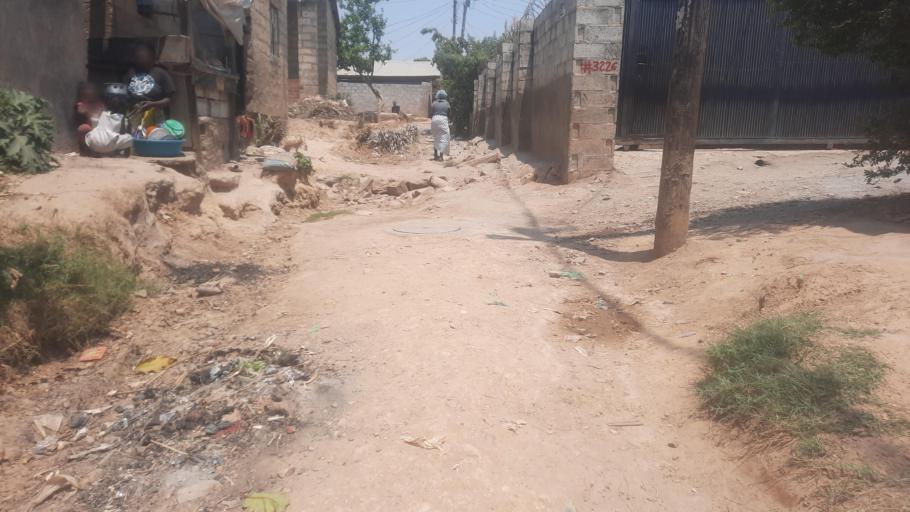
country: ZM
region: Lusaka
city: Lusaka
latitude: -15.4021
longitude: 28.3728
